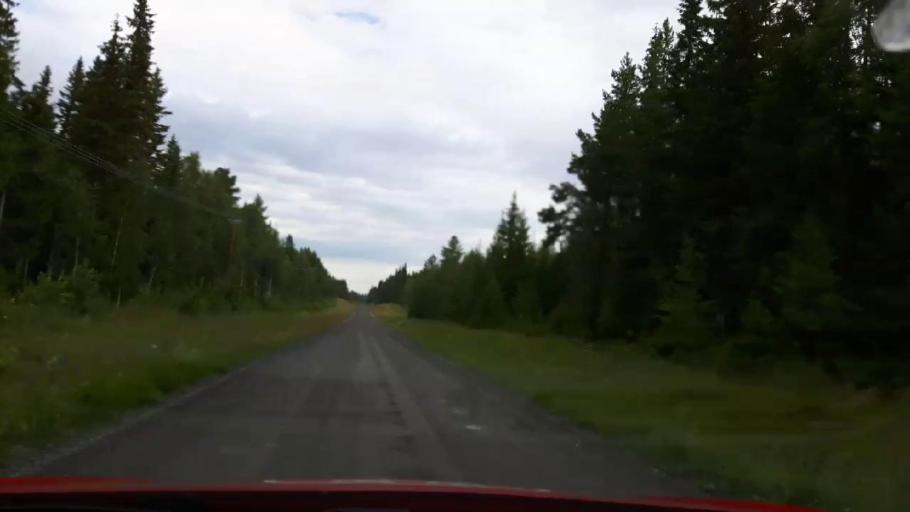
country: SE
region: Jaemtland
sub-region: Stroemsunds Kommun
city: Stroemsund
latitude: 63.5071
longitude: 15.3366
